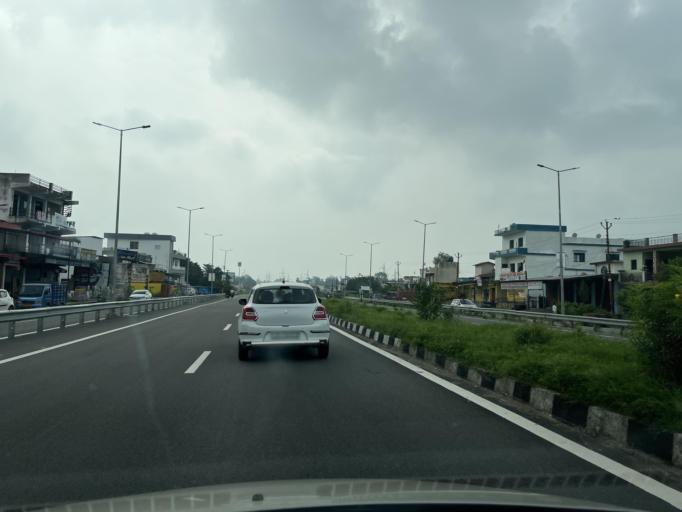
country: IN
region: Uttarakhand
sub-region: Dehradun
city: Raiwala
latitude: 30.0755
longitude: 78.1984
